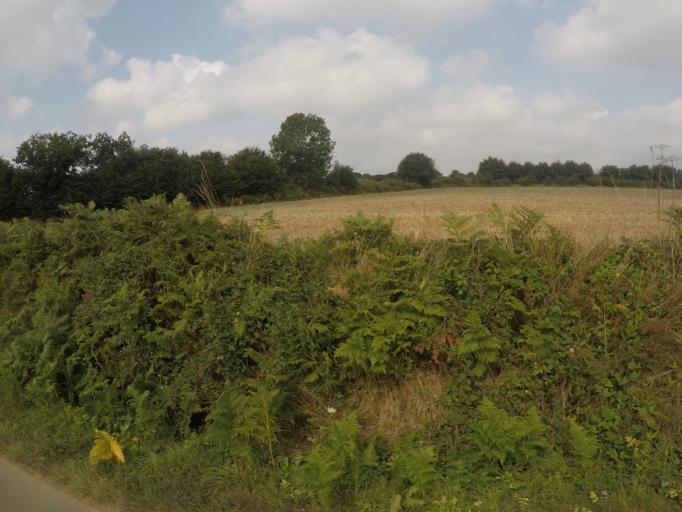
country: FR
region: Brittany
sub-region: Departement des Cotes-d'Armor
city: Plelo
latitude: 48.5567
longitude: -2.9369
